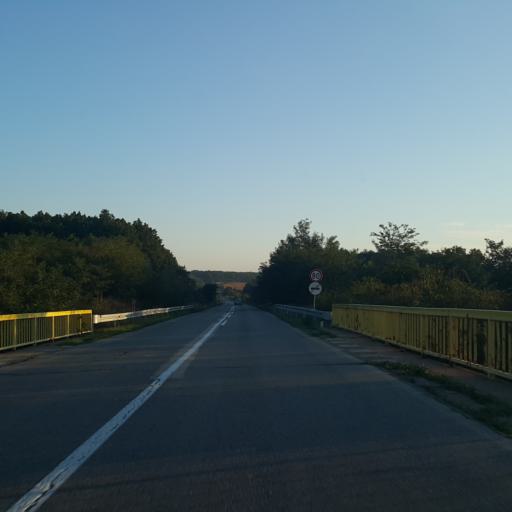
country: RS
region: Central Serbia
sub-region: Borski Okrug
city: Negotin
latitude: 44.1475
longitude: 22.3543
